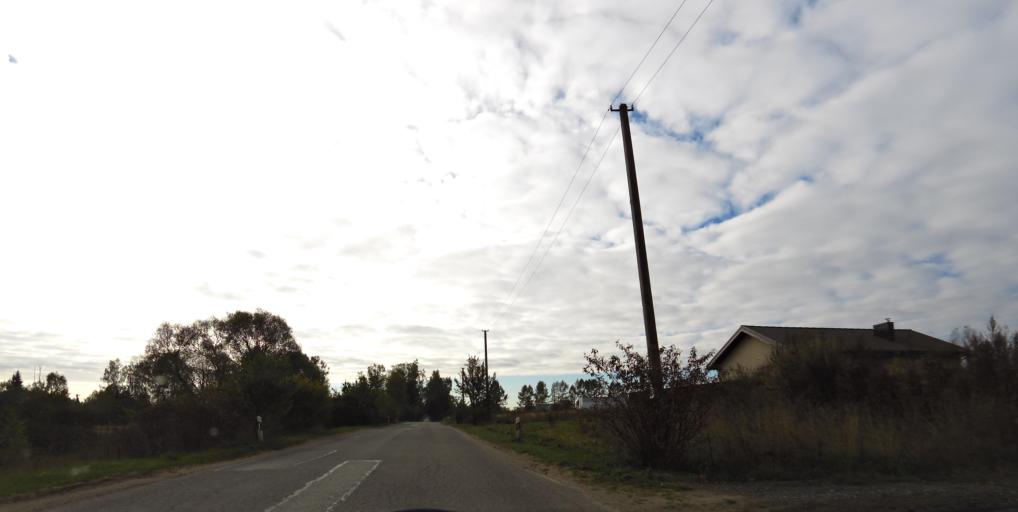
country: LT
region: Vilnius County
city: Pilaite
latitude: 54.7178
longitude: 25.1588
